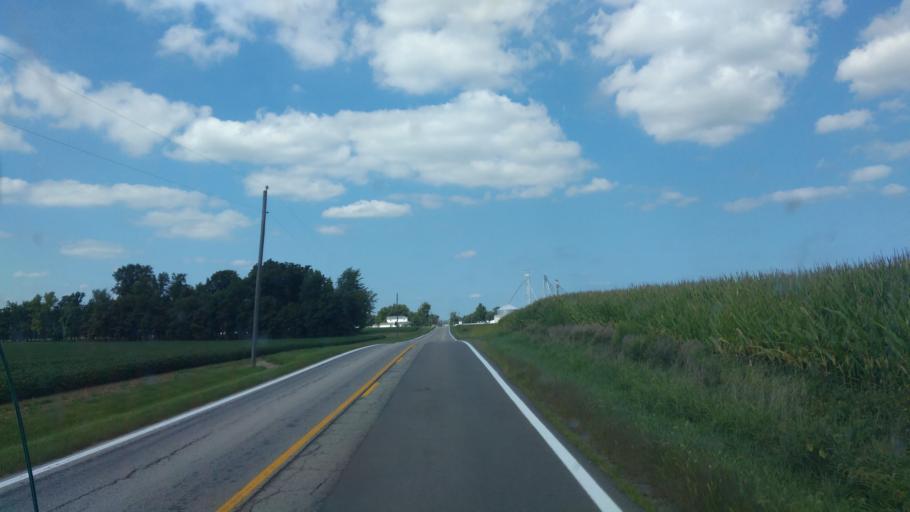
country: US
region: Ohio
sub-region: Union County
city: Marysville
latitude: 40.3758
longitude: -83.4541
